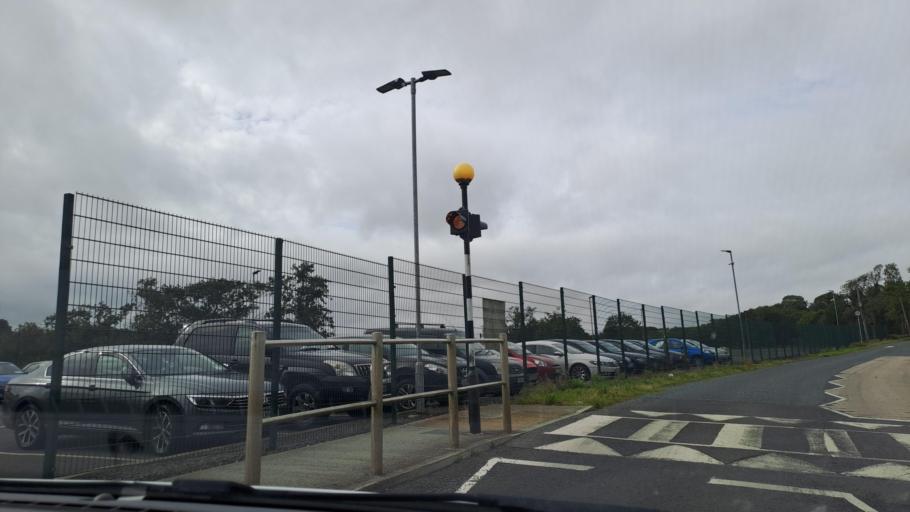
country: IE
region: Ulster
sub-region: An Cabhan
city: Bailieborough
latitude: 53.9962
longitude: -6.9032
